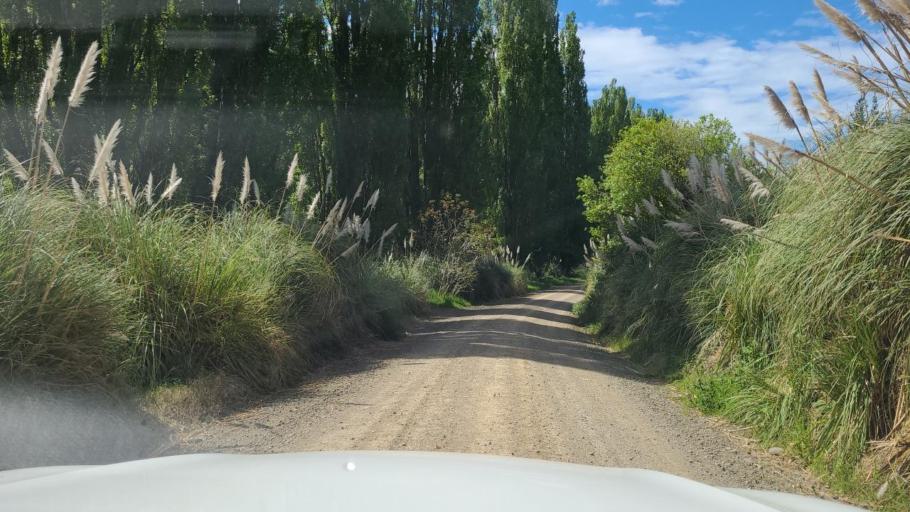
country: NZ
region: Hawke's Bay
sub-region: Napier City
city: Napier
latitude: -39.1396
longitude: 177.0181
